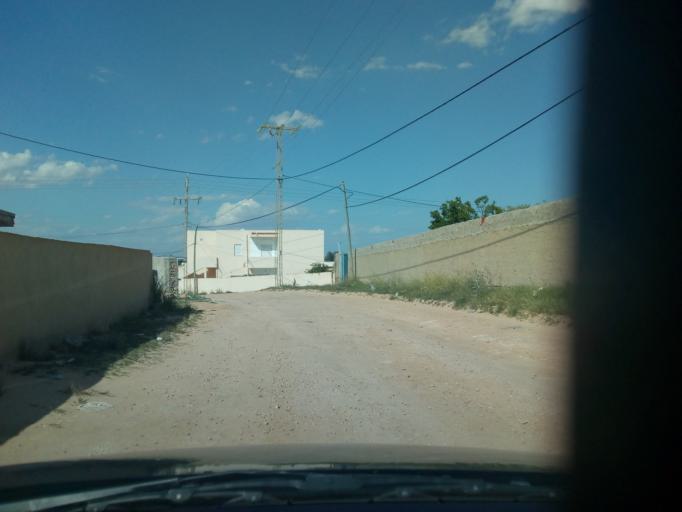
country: TN
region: Safaqis
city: Sfax
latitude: 34.7291
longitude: 10.6053
